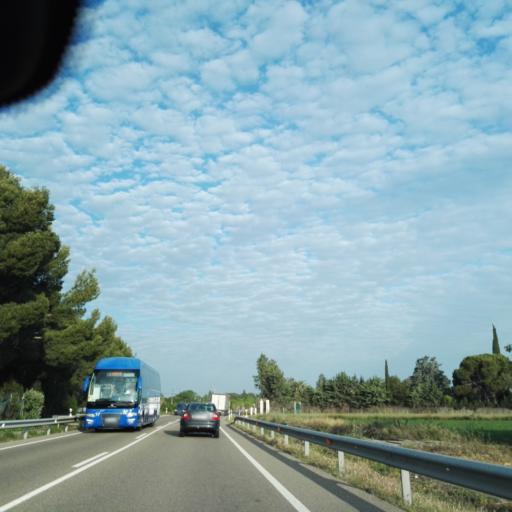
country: ES
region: Aragon
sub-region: Provincia de Zaragoza
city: Utebo
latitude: 41.6634
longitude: -0.9882
